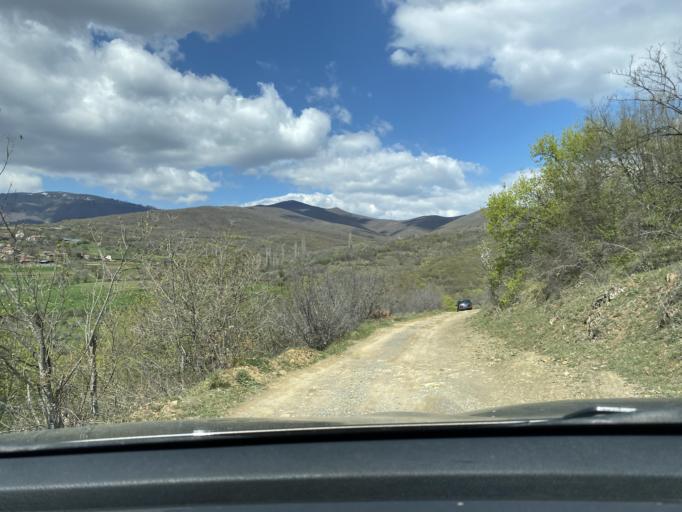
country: MK
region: Caska
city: Caska
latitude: 41.7336
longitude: 21.6497
